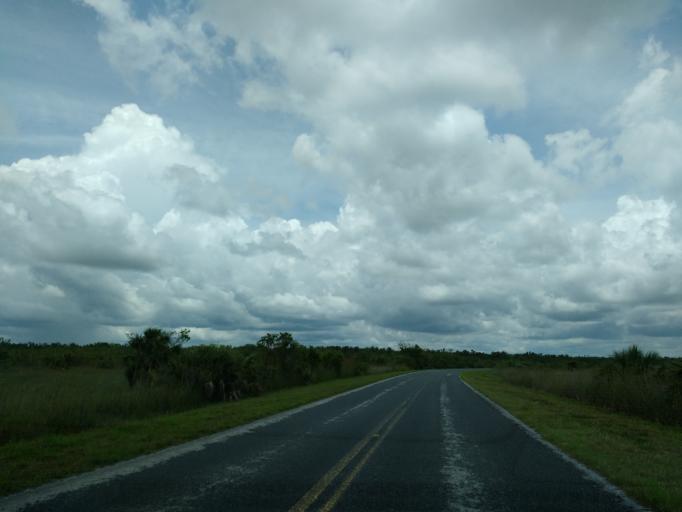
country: US
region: Florida
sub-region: Miami-Dade County
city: Florida City
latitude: 25.3894
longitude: -80.6146
